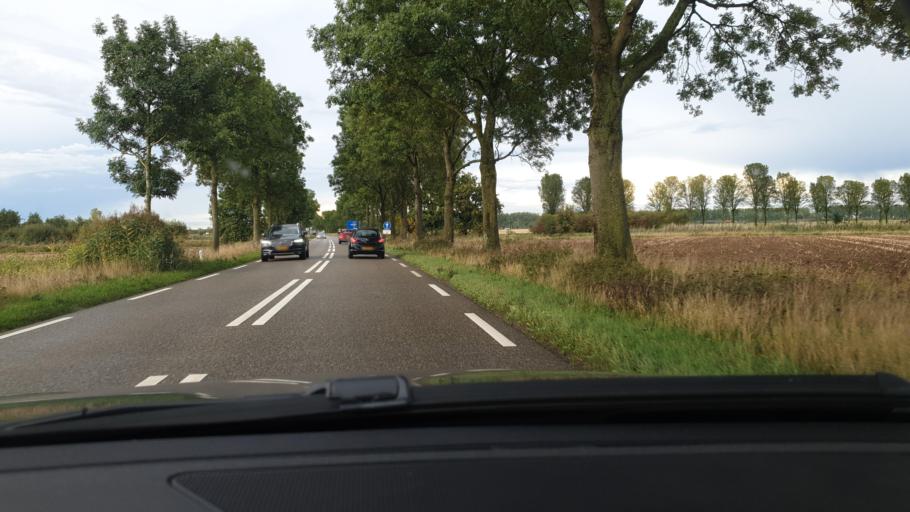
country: NL
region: North Brabant
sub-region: Gemeente Oss
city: Berghem
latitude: 51.7975
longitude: 5.5603
